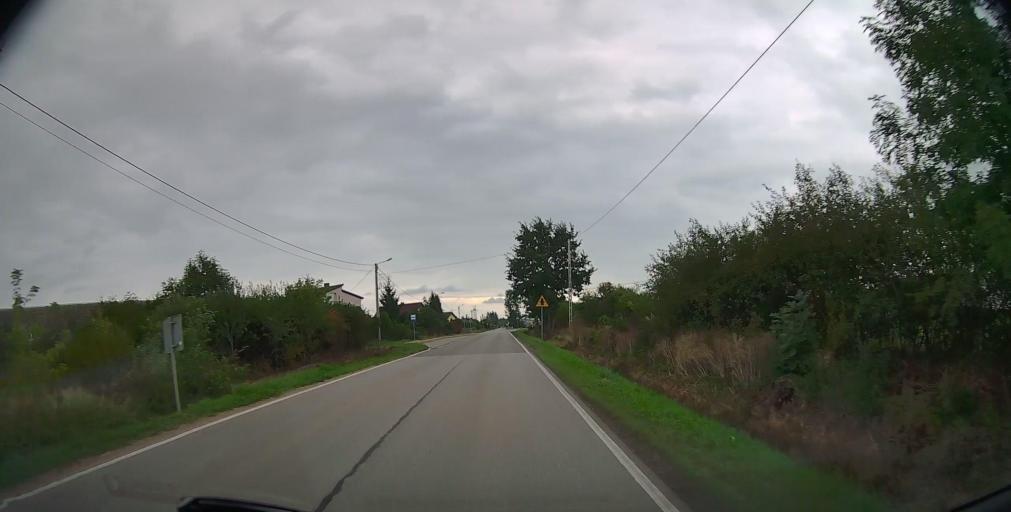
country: PL
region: Masovian Voivodeship
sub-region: Powiat radomski
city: Jedlinsk
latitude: 51.4500
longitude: 21.0854
